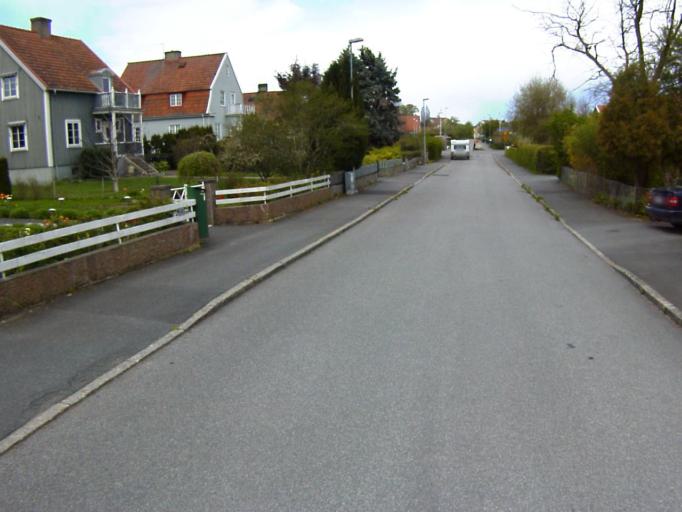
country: SE
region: Skane
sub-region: Kristianstads Kommun
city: Kristianstad
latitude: 56.0389
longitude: 14.1698
